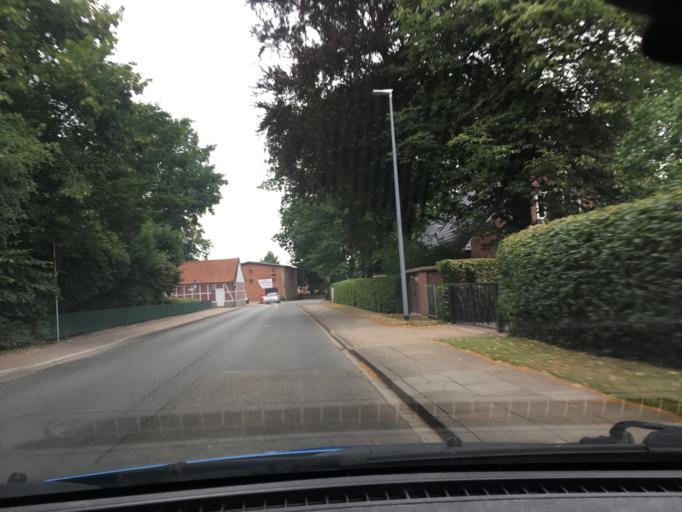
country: DE
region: Lower Saxony
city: Tostedt
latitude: 53.2808
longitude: 9.7348
